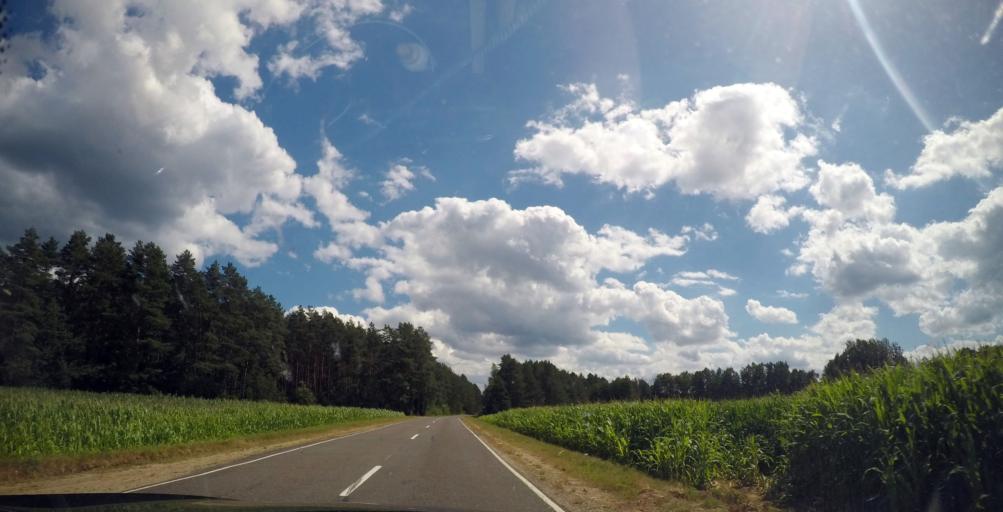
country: LT
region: Alytaus apskritis
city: Druskininkai
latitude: 53.8702
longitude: 24.1613
